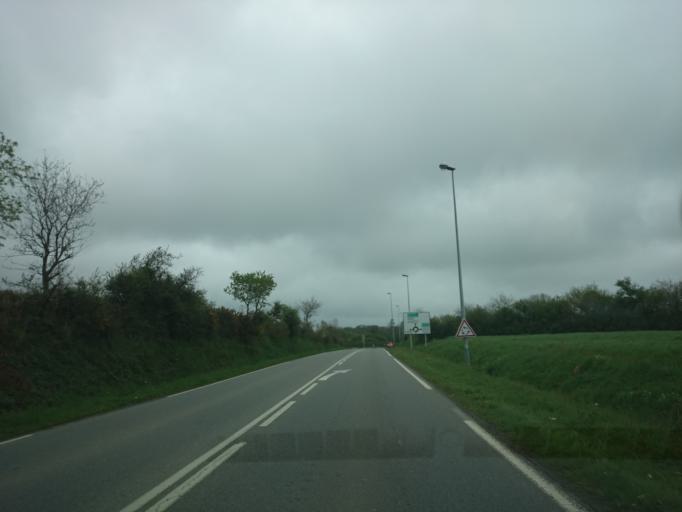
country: FR
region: Brittany
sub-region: Departement du Finistere
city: Gouesnou
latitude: 48.4453
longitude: -4.4592
